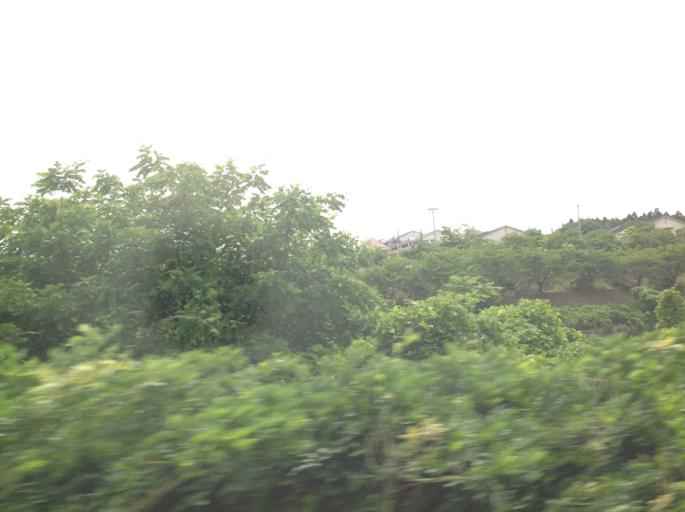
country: JP
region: Miyagi
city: Tomiya
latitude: 38.3357
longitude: 140.8557
